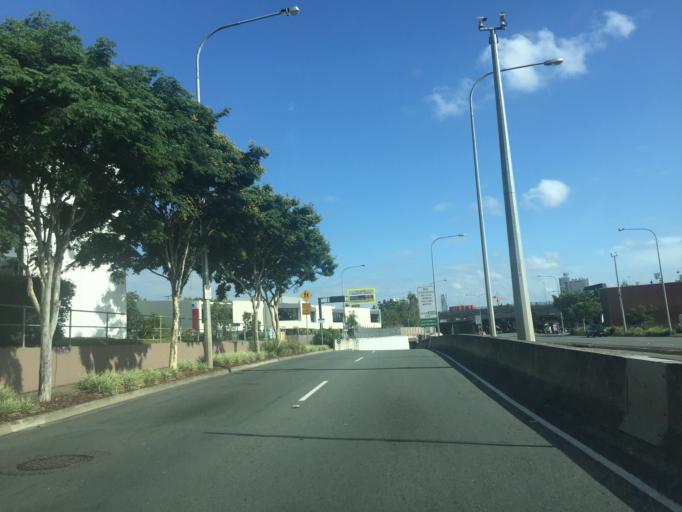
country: AU
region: Queensland
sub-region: Brisbane
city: Woolloongabba
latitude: -27.4951
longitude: 153.0345
